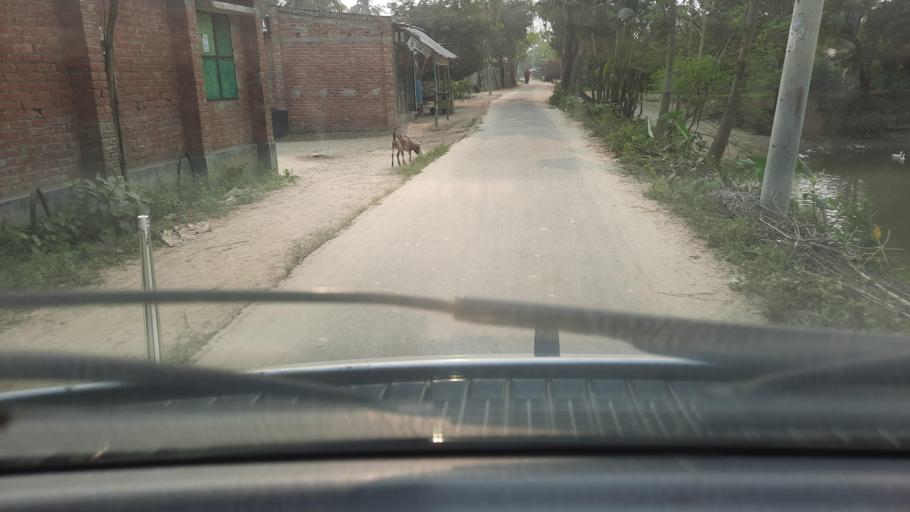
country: BD
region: Khulna
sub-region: Chuadanga
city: Nowlamary
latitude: 23.6042
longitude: 88.8581
